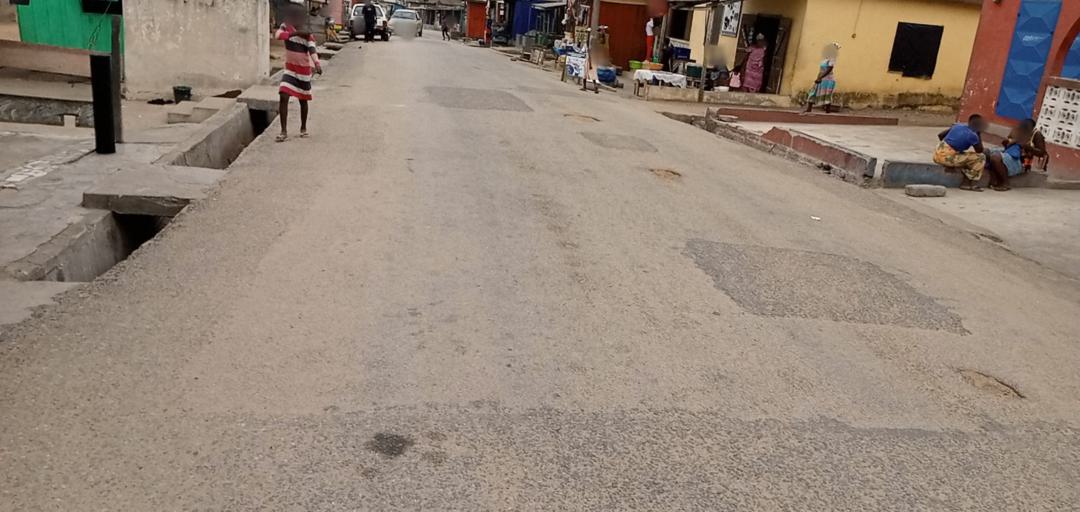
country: GH
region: Central
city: Winneba
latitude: 5.3458
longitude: -0.6212
